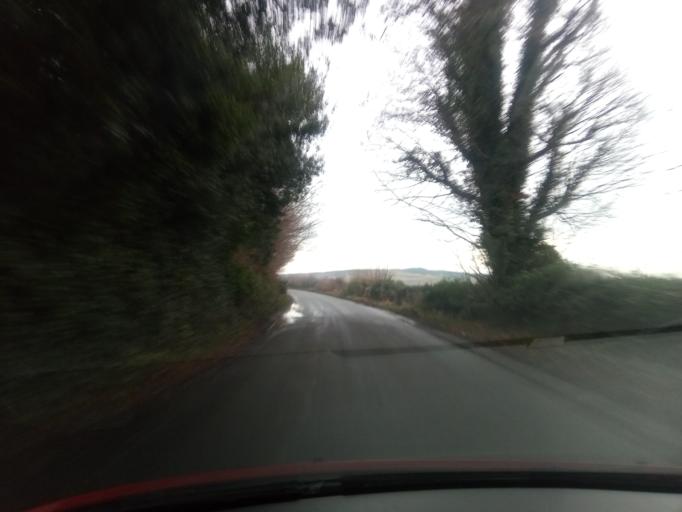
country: GB
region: England
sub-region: Northumberland
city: Whittingham
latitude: 55.4855
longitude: -1.8933
